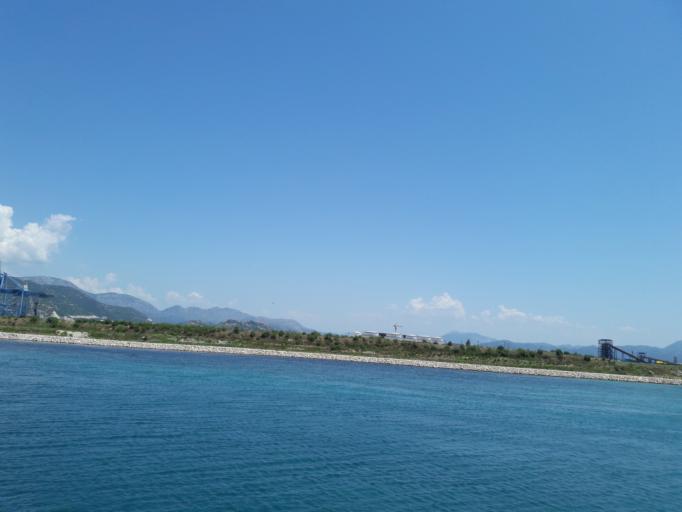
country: HR
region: Dubrovacko-Neretvanska
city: Komin
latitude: 43.0406
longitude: 17.4196
